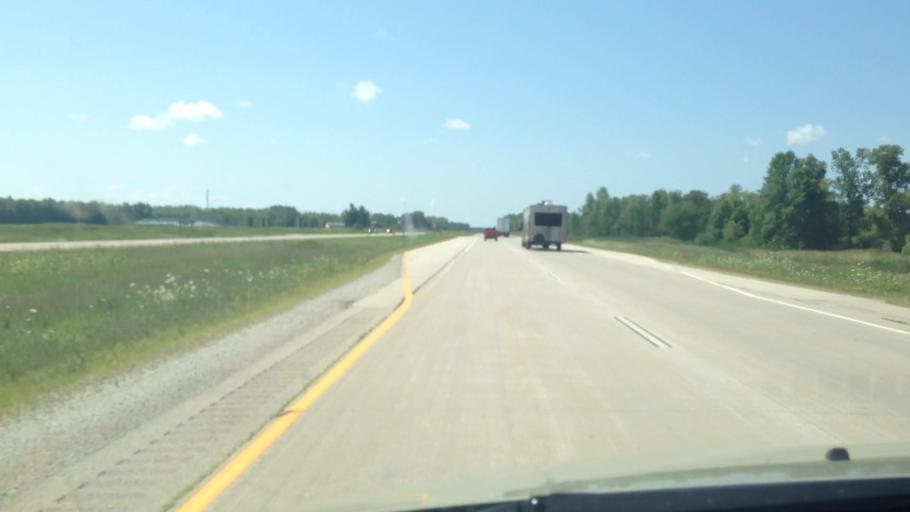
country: US
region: Wisconsin
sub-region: Oconto County
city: Oconto
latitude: 44.9925
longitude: -87.8568
